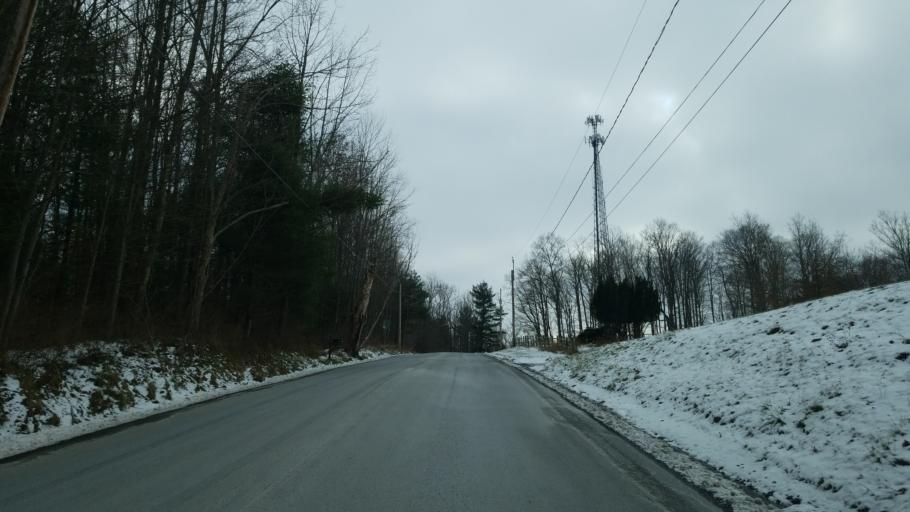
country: US
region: Pennsylvania
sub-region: Clearfield County
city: Sandy
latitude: 41.1050
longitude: -78.7599
